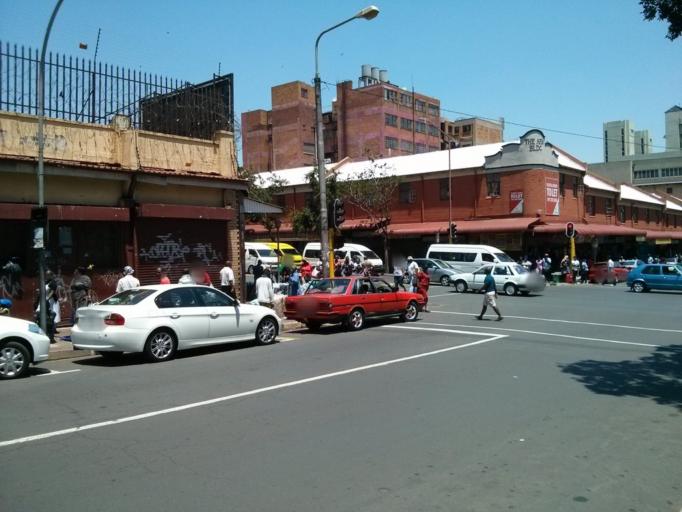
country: ZA
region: Gauteng
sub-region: City of Johannesburg Metropolitan Municipality
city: Johannesburg
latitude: -26.2045
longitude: 28.0356
